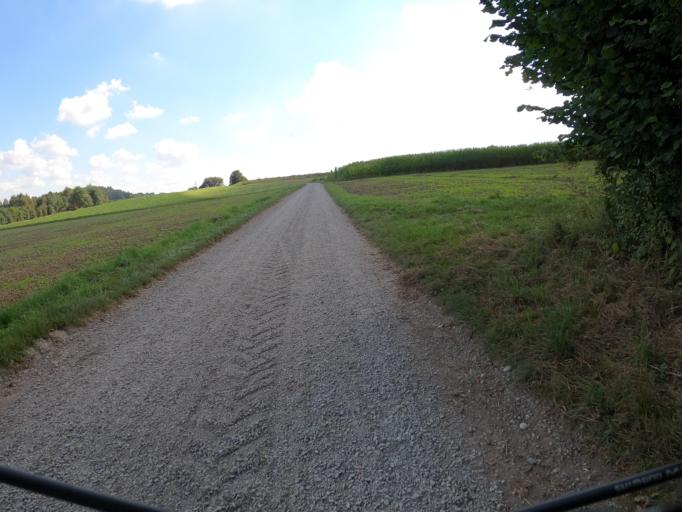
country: DE
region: Bavaria
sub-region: Swabia
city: Pfaffenhofen an der Roth
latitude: 48.3705
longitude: 10.1829
